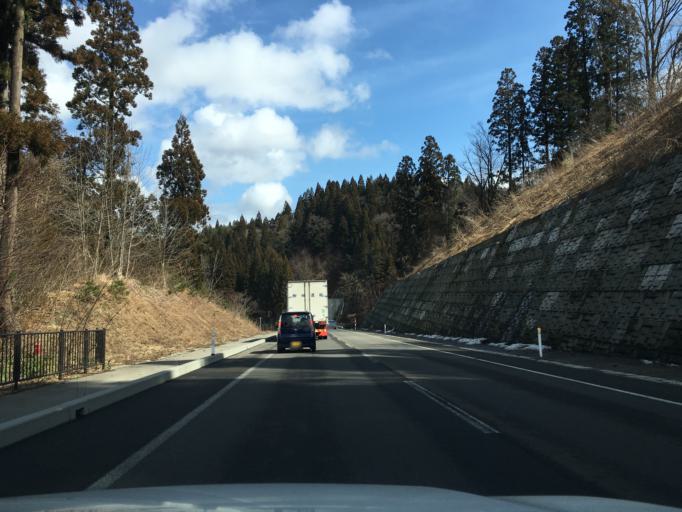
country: JP
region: Akita
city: Takanosu
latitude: 40.1122
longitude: 140.3698
